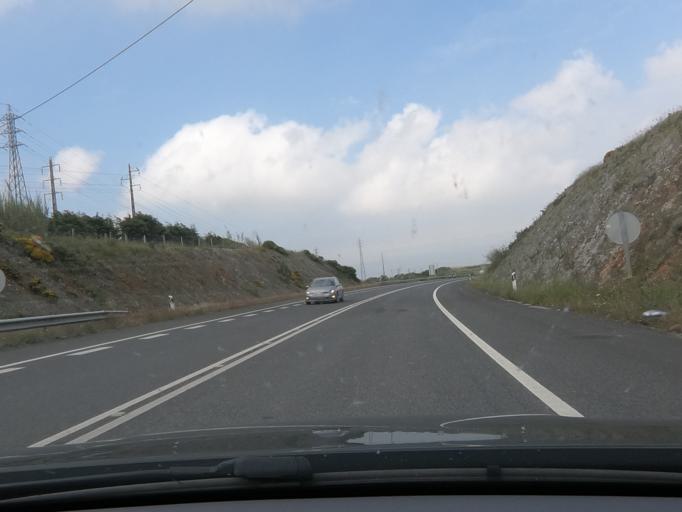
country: PT
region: Leiria
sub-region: Peniche
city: Atouguia da Baleia
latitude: 39.3238
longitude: -9.2757
